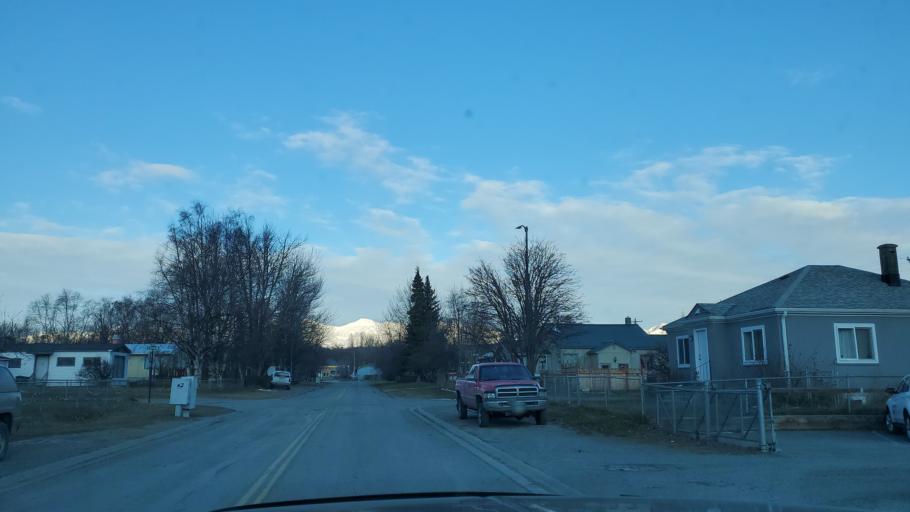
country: US
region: Alaska
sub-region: Matanuska-Susitna Borough
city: Palmer
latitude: 61.6040
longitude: -149.1165
